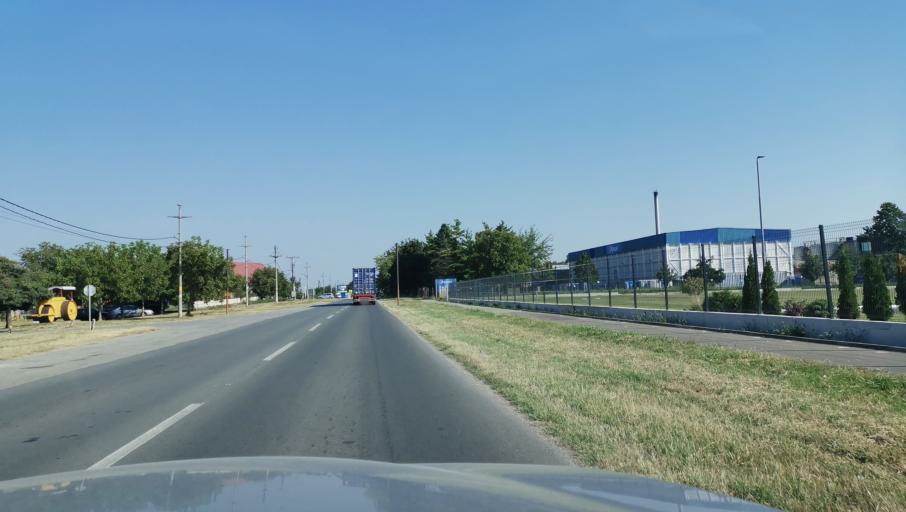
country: RS
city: Dobanovci
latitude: 44.8130
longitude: 20.2401
